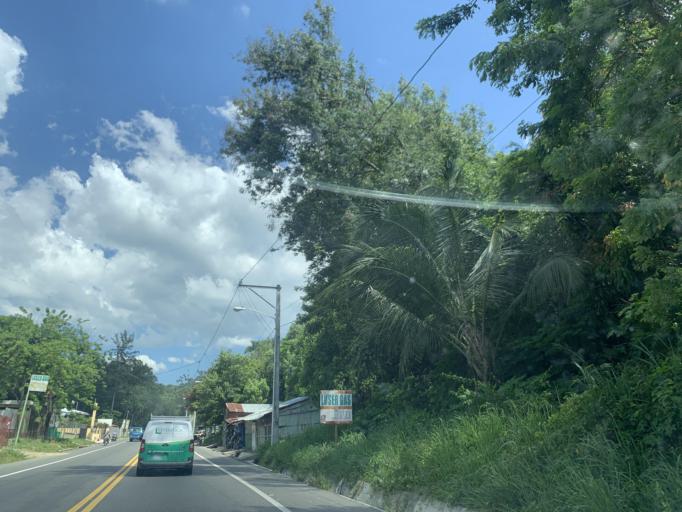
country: DO
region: Puerto Plata
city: Altamira
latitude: 19.6691
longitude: -70.8321
